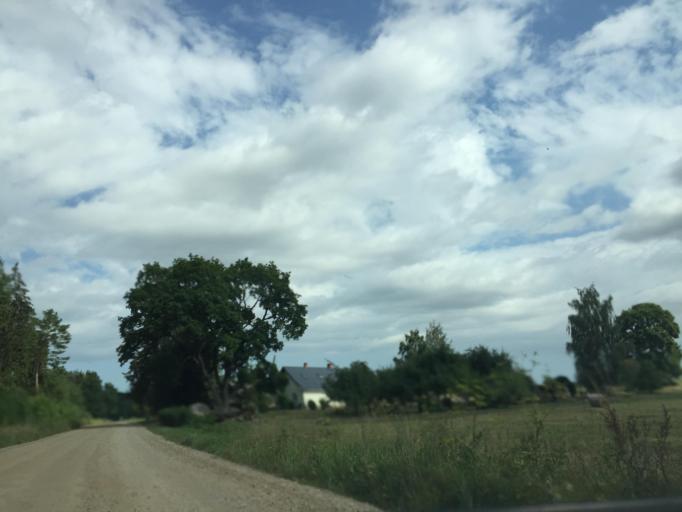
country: LV
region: Kandava
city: Kandava
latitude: 57.0252
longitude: 22.8186
